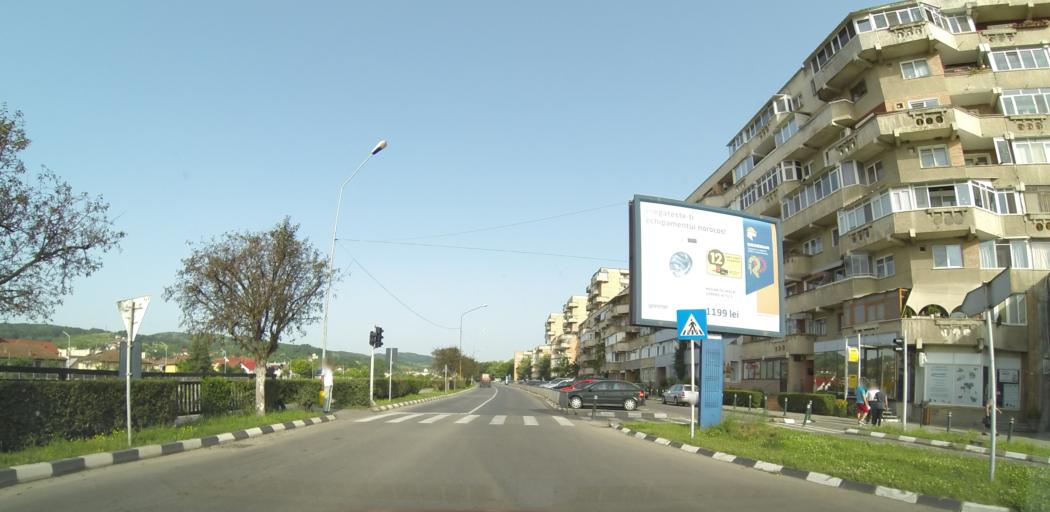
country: RO
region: Valcea
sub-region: Municipiul Ramnicu Valcea
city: Ramnicu Valcea
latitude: 45.1013
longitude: 24.3617
